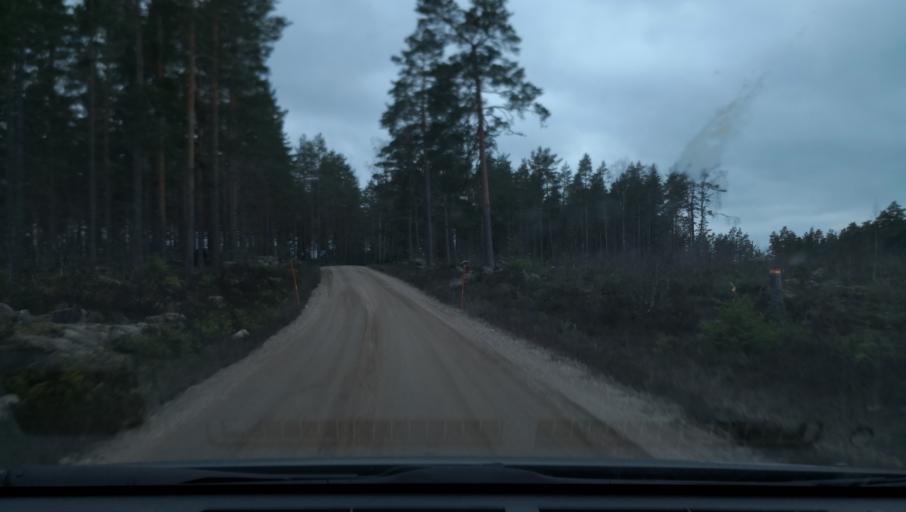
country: SE
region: OErebro
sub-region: Lindesbergs Kommun
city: Fellingsbro
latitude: 59.6136
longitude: 15.5823
